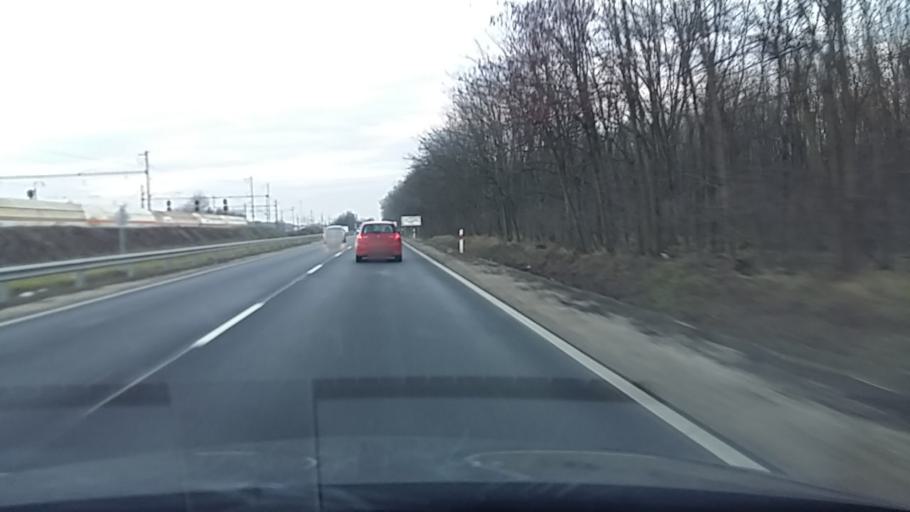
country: HU
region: Hajdu-Bihar
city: Debrecen
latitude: 47.5802
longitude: 21.6546
